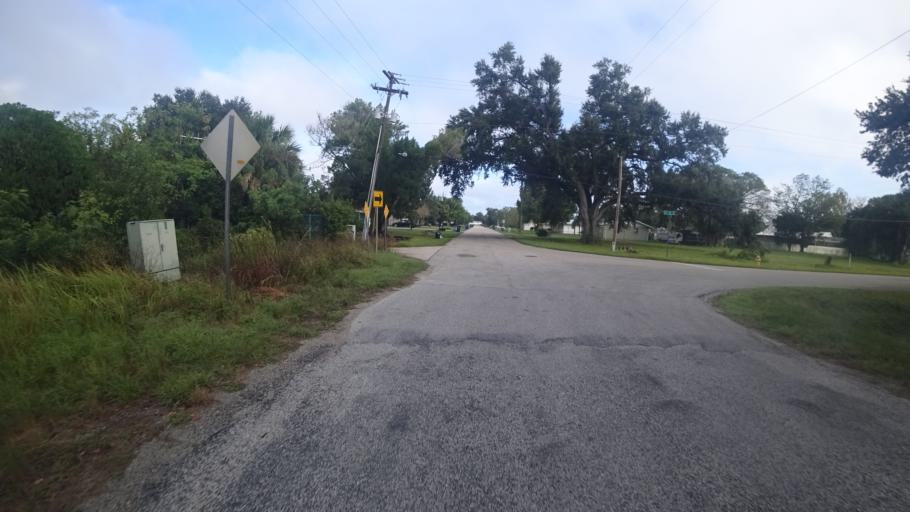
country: US
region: Florida
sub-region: Manatee County
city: Ellenton
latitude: 27.5353
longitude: -82.4827
